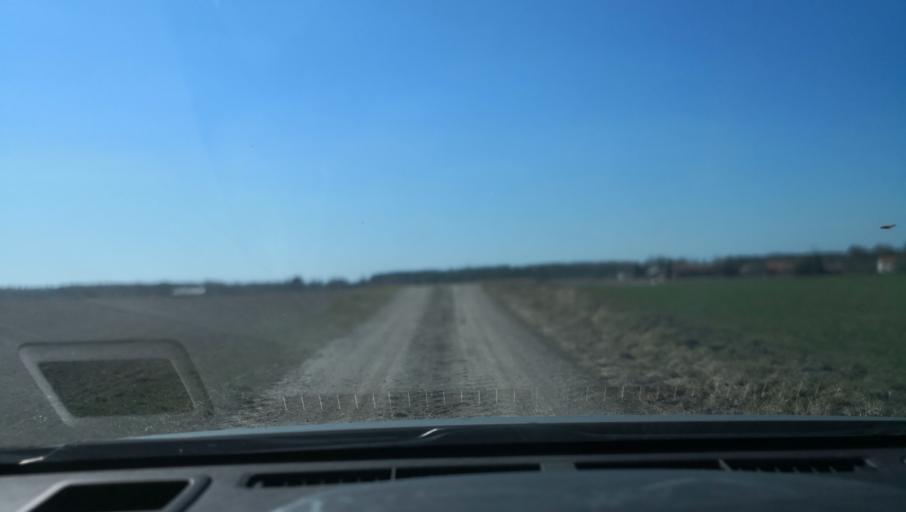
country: SE
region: Vaestmanland
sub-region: Sala Kommun
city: Sala
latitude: 59.8540
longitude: 16.5441
